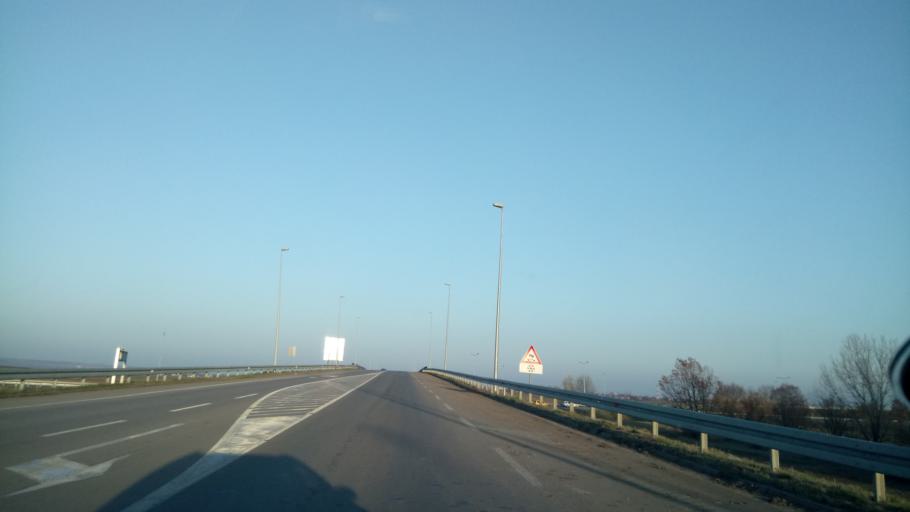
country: RS
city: Novi Karlovci
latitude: 45.0711
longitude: 20.1474
